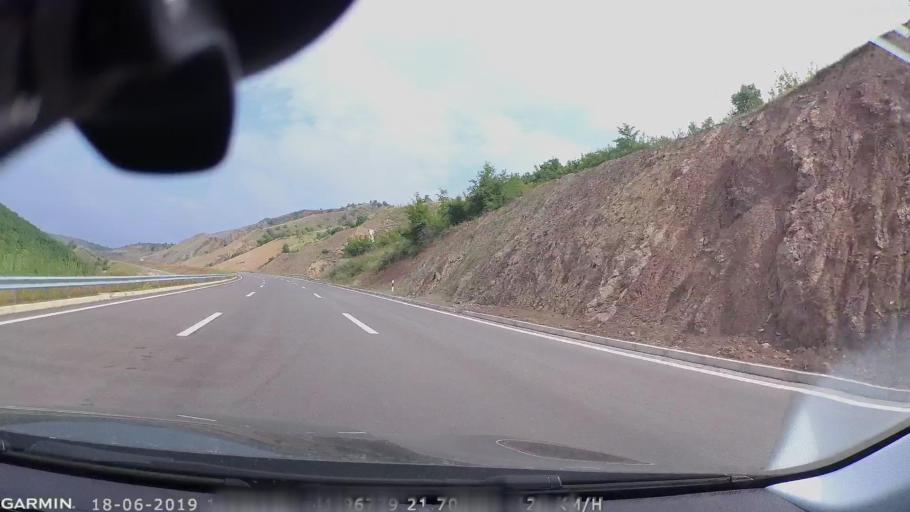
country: MK
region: Petrovec
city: Sredno Konjare
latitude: 41.9456
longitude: 21.7947
